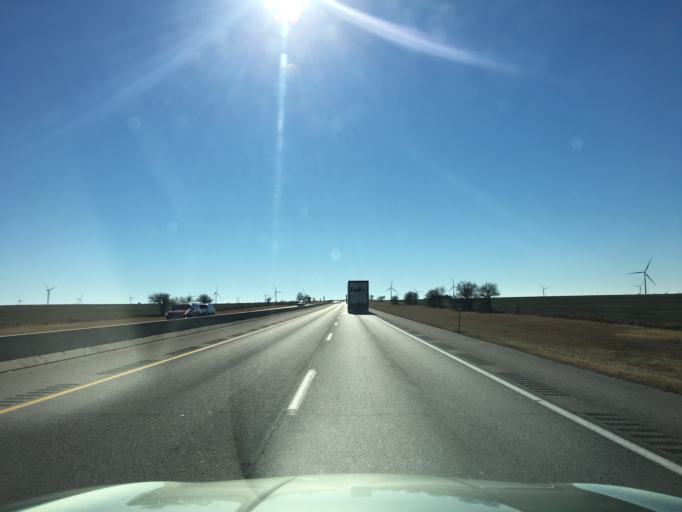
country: US
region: Kansas
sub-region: Sumner County
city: Wellington
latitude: 37.1717
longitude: -97.3396
